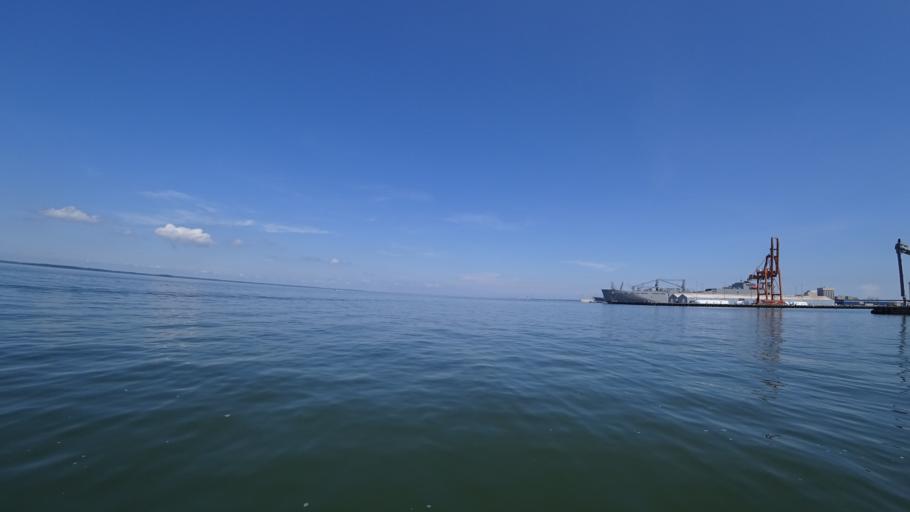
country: US
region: Virginia
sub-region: City of Newport News
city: Newport News
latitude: 36.9650
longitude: -76.4308
